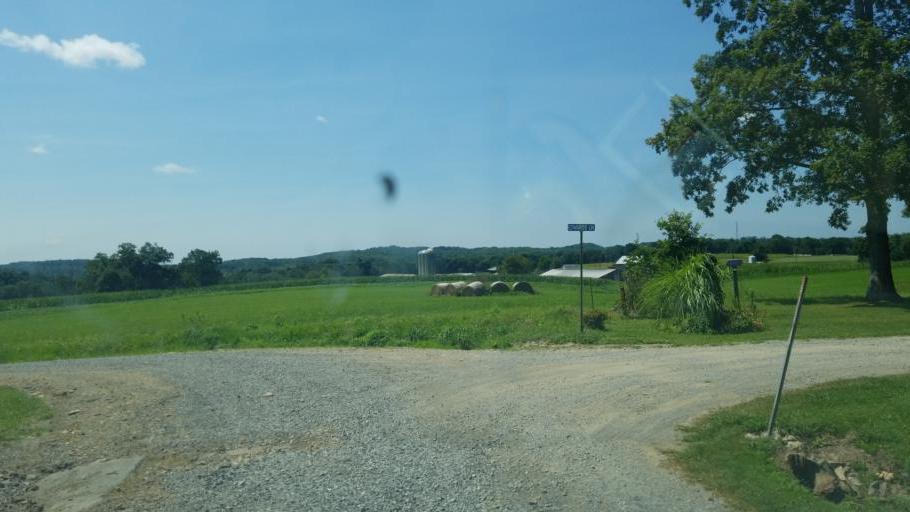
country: US
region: Pennsylvania
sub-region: Clarion County
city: Knox
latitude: 41.2009
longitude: -79.5497
